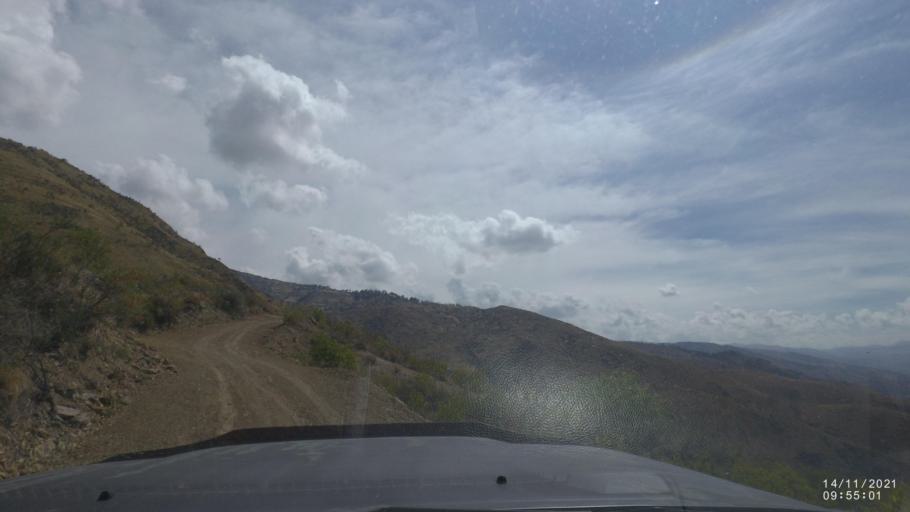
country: BO
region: Cochabamba
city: Cochabamba
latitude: -17.3584
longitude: -66.0876
